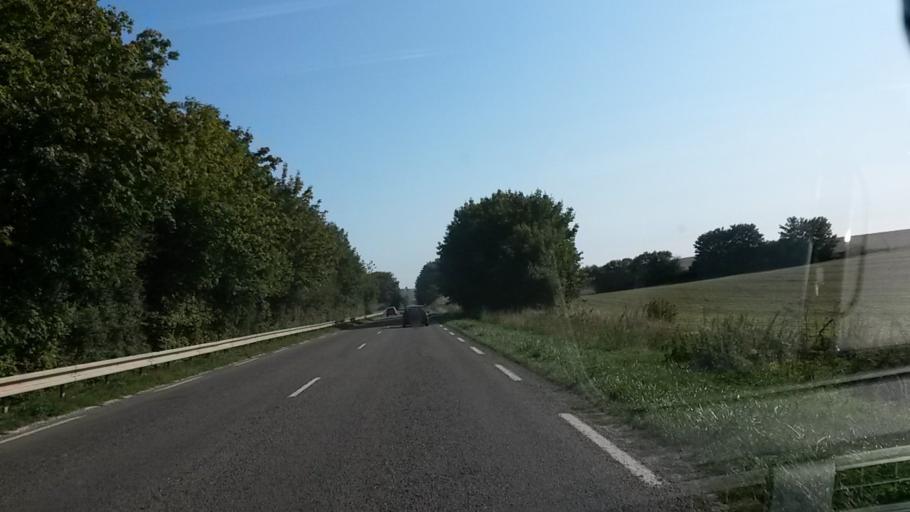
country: FR
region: Picardie
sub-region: Departement de l'Aisne
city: Guise
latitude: 49.8750
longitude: 3.5815
